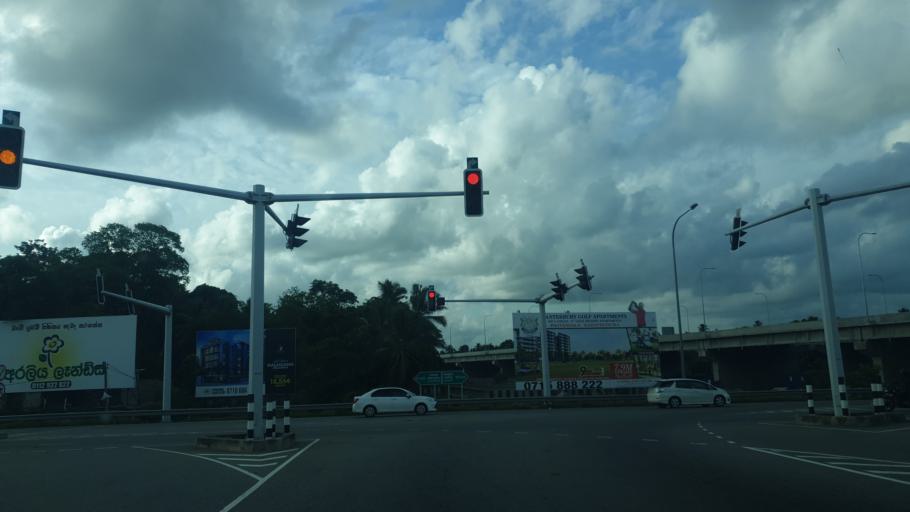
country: LK
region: Western
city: Kelaniya
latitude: 7.0022
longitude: 79.9601
